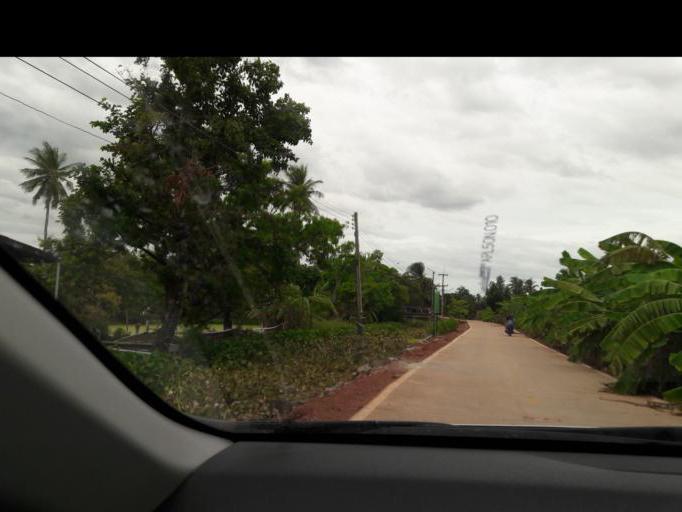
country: TH
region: Ratchaburi
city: Damnoen Saduak
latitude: 13.5416
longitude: 99.9748
